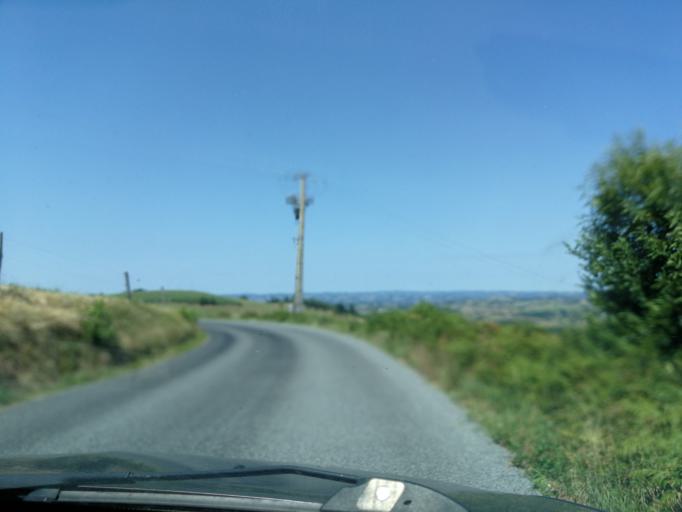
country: FR
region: Midi-Pyrenees
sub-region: Departement de l'Aveyron
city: Livinhac-le-Haut
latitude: 44.6641
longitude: 2.3029
